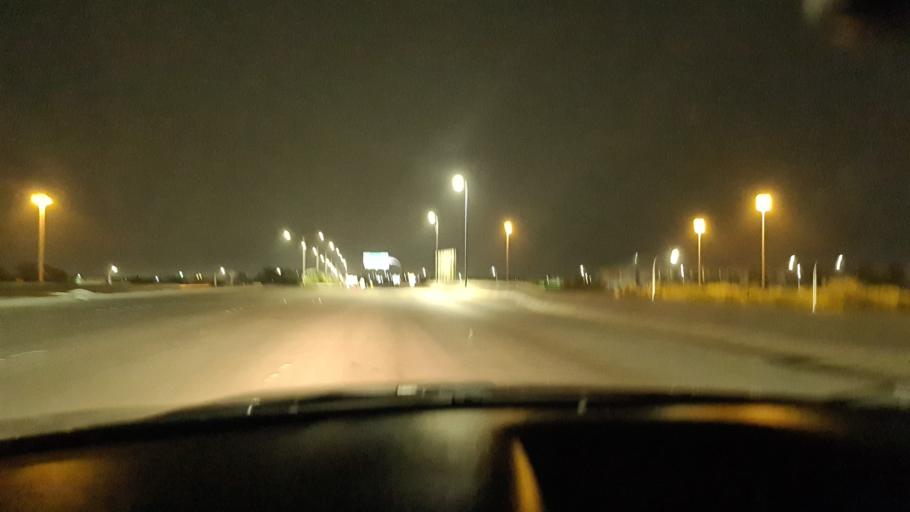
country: SA
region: Eastern Province
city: Al Jubayl
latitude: 27.1367
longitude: 49.5579
